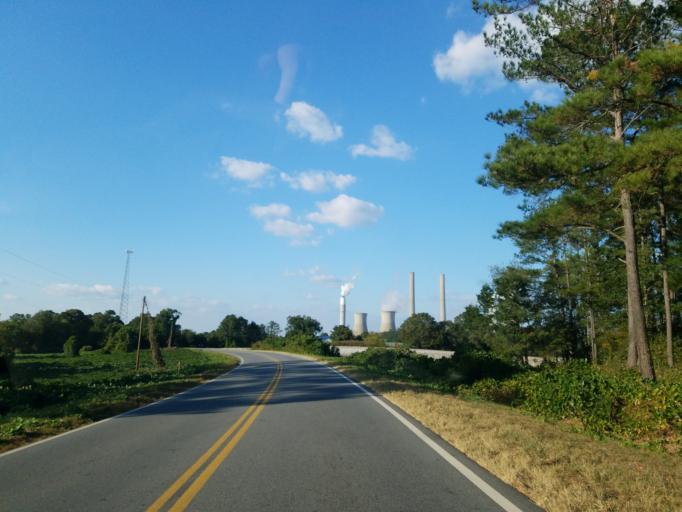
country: US
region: Georgia
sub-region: Bartow County
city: Euharlee
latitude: 34.1058
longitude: -84.9264
